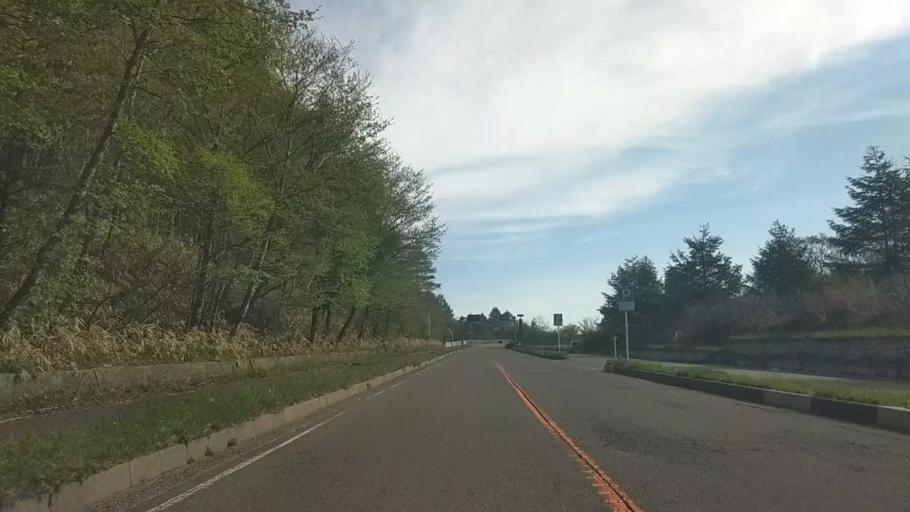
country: JP
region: Yamanashi
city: Nirasaki
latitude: 35.9415
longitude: 138.4500
